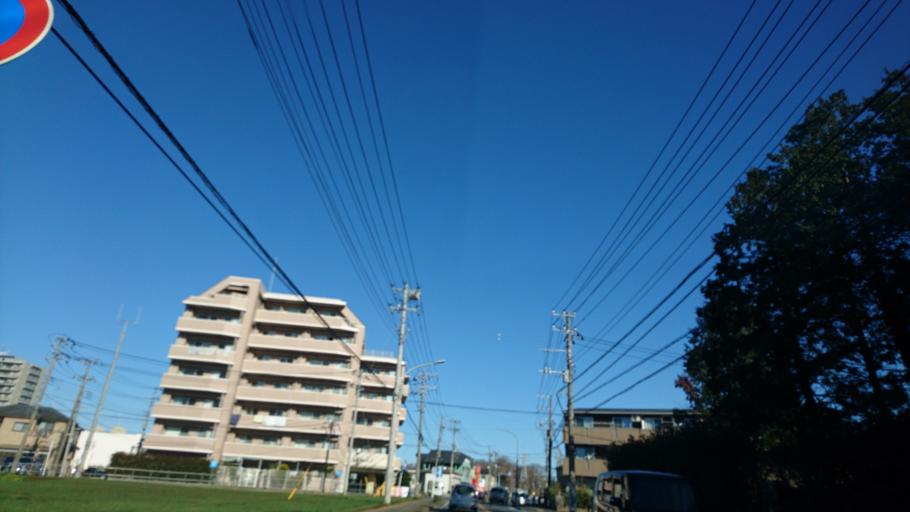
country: JP
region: Chiba
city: Chiba
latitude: 35.5864
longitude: 140.1426
